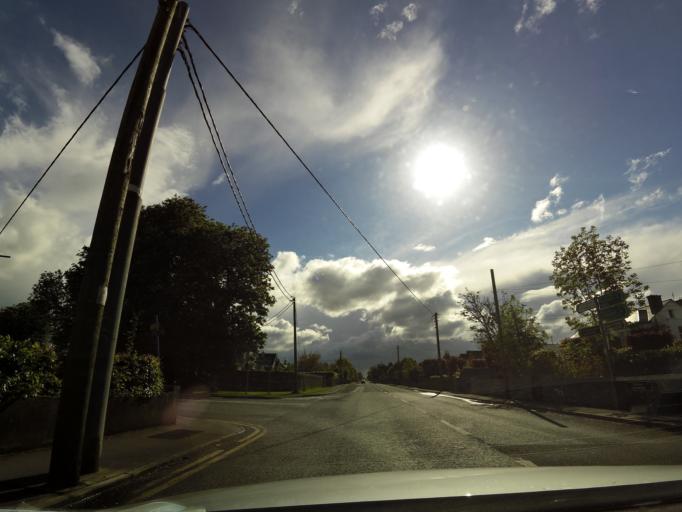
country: IE
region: Munster
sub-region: North Tipperary
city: Templemore
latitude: 52.7936
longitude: -7.8437
